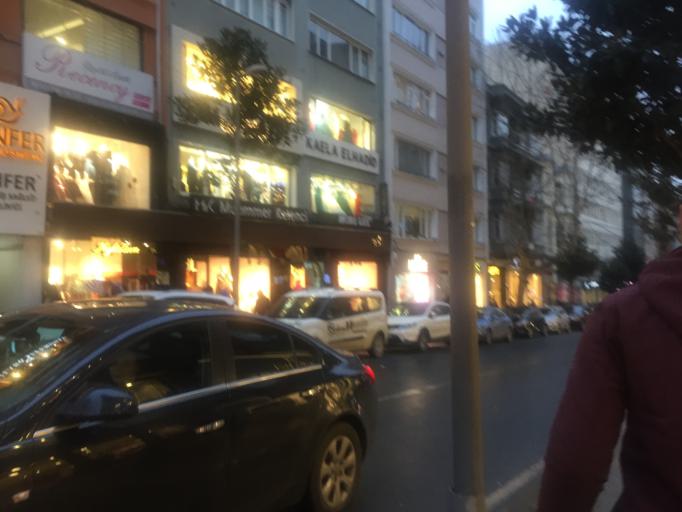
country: TR
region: Istanbul
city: Sisli
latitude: 41.0527
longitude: 28.9903
